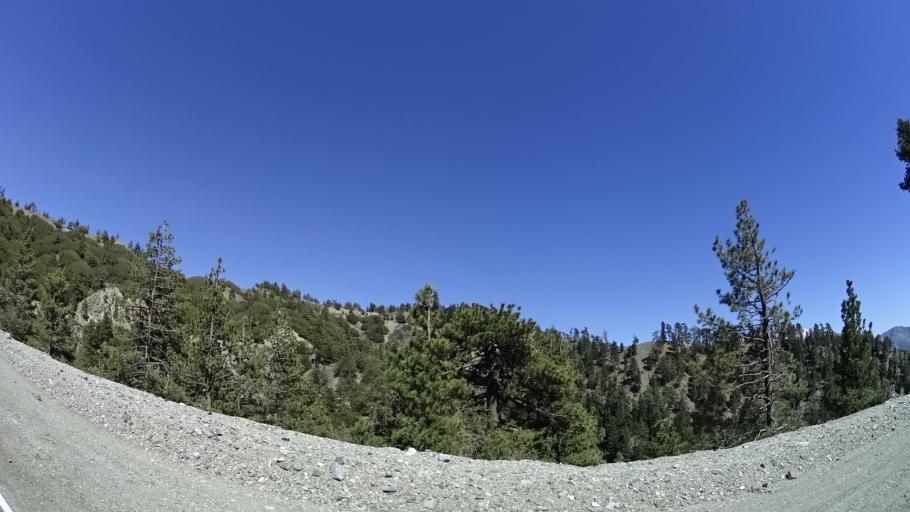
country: US
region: California
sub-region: San Bernardino County
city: Wrightwood
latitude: 34.3777
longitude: -117.7314
